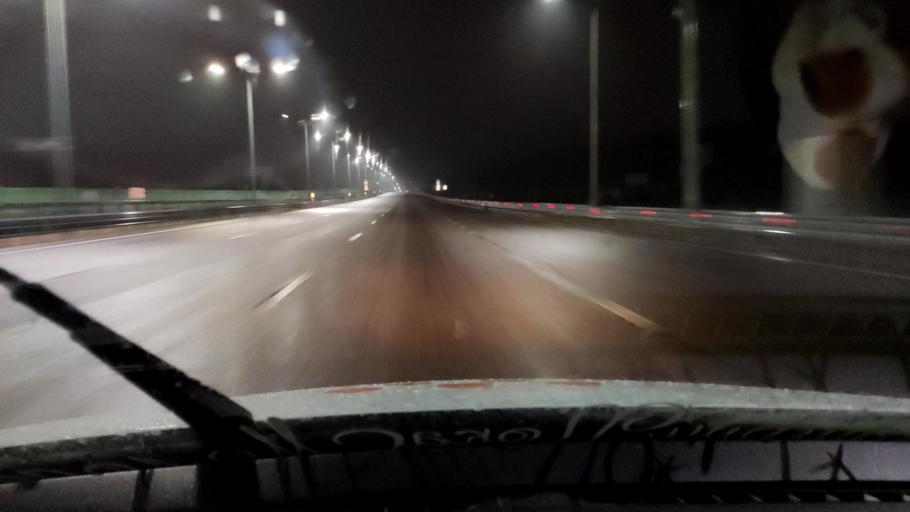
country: RU
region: Voronezj
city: Somovo
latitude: 51.7406
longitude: 39.3077
